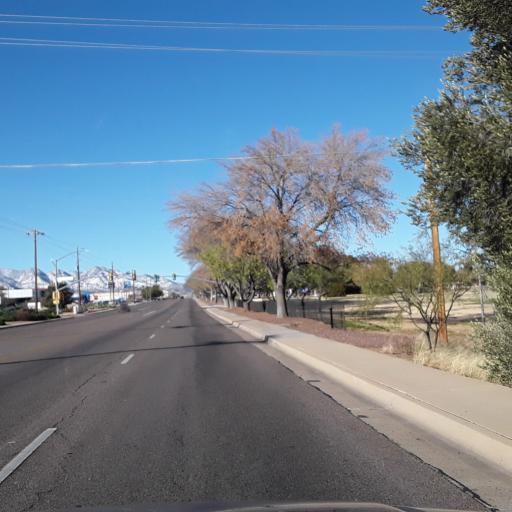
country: US
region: Arizona
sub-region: Cochise County
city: Sierra Vista
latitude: 31.5547
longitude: -110.2655
